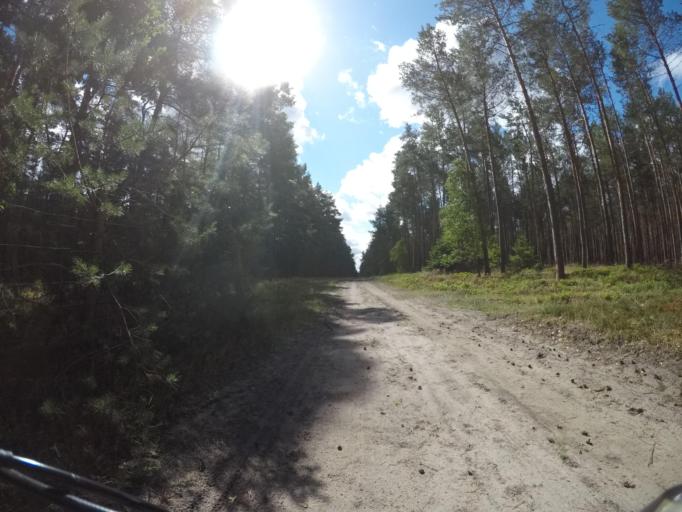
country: DE
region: Lower Saxony
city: Hitzacker
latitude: 53.2297
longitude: 11.0278
